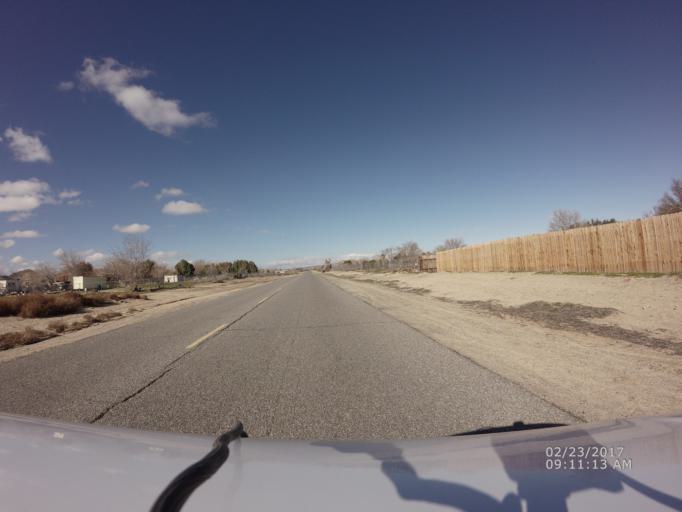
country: US
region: California
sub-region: Los Angeles County
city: Lake Los Angeles
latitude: 34.6239
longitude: -117.8192
